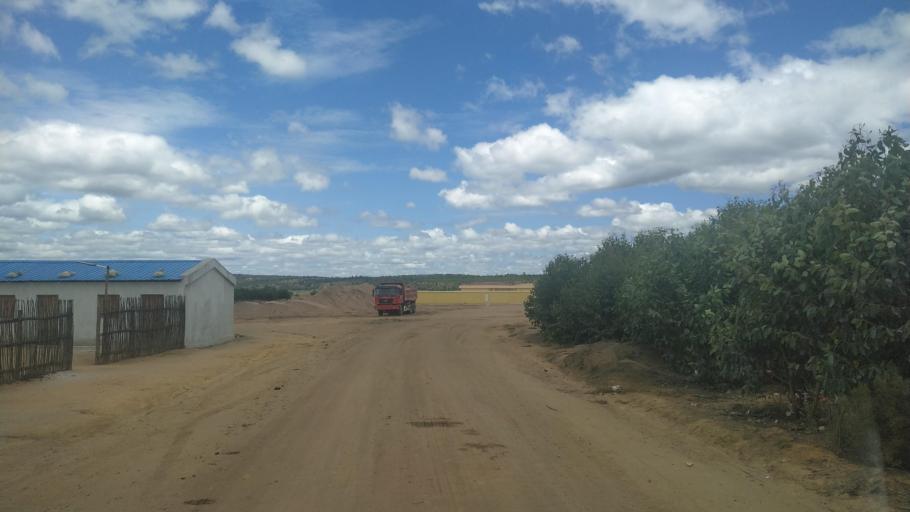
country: MG
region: Analamanga
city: Anjozorobe
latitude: -18.2757
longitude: 48.2642
